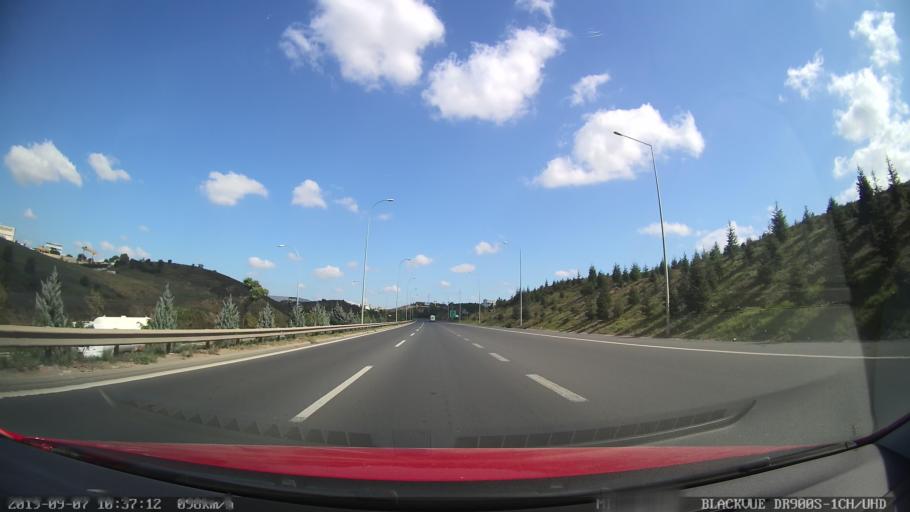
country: TR
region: Kocaeli
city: Balcik
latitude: 40.8432
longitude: 29.3742
